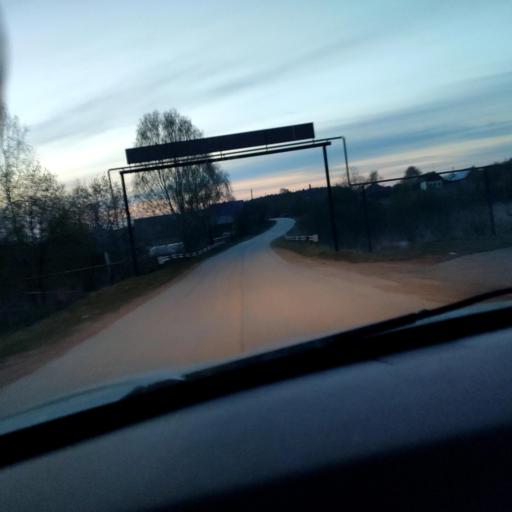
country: RU
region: Perm
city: Kukushtan
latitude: 57.4658
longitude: 56.5371
